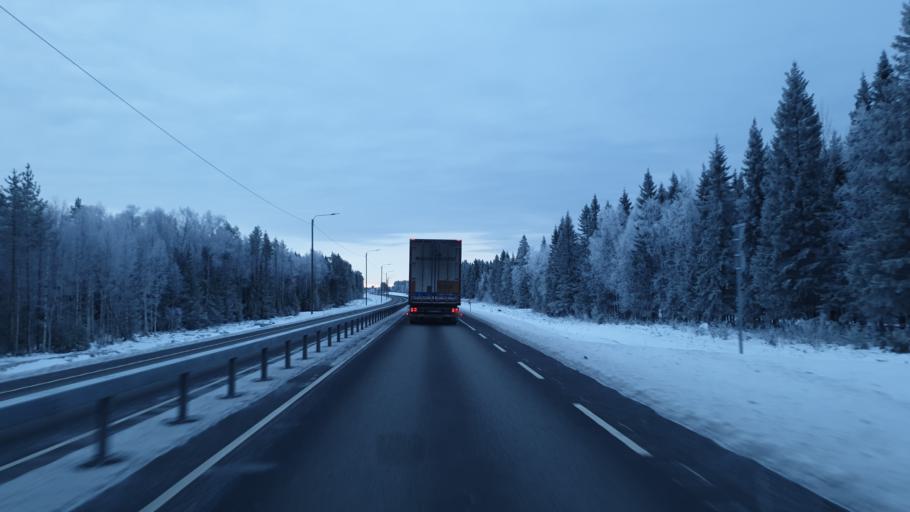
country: FI
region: Northern Ostrobothnia
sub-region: Oulunkaari
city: Kuivaniemi
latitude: 65.6154
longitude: 25.1654
